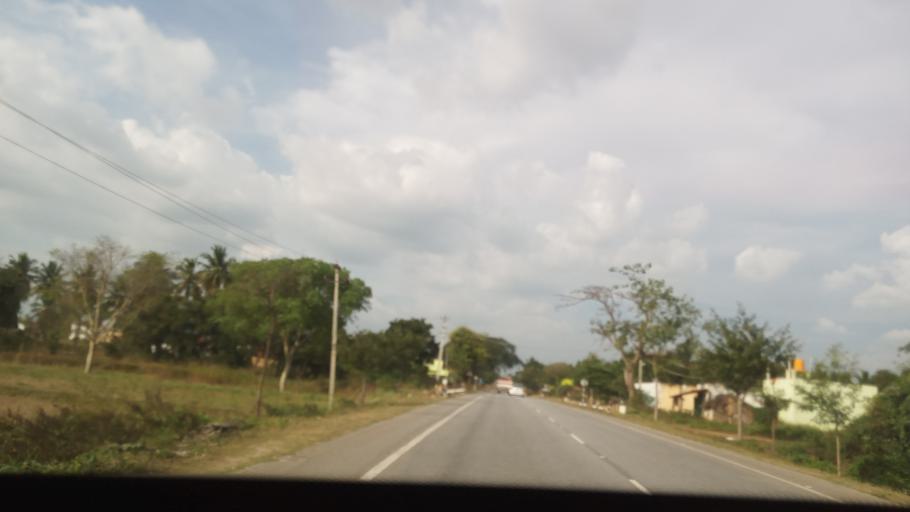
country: IN
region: Karnataka
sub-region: Tumkur
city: Kunigal
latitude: 12.8635
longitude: 77.0398
